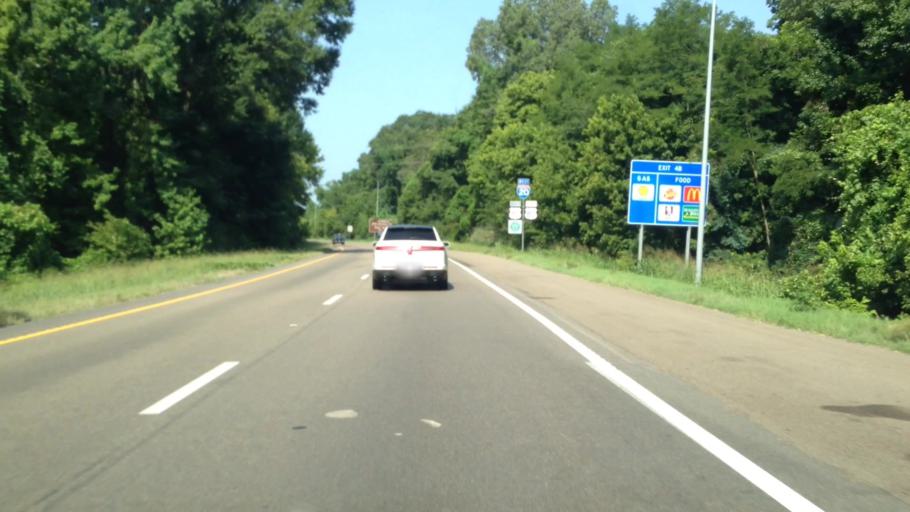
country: US
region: Mississippi
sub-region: Warren County
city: Beechwood
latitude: 32.3479
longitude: -90.8348
